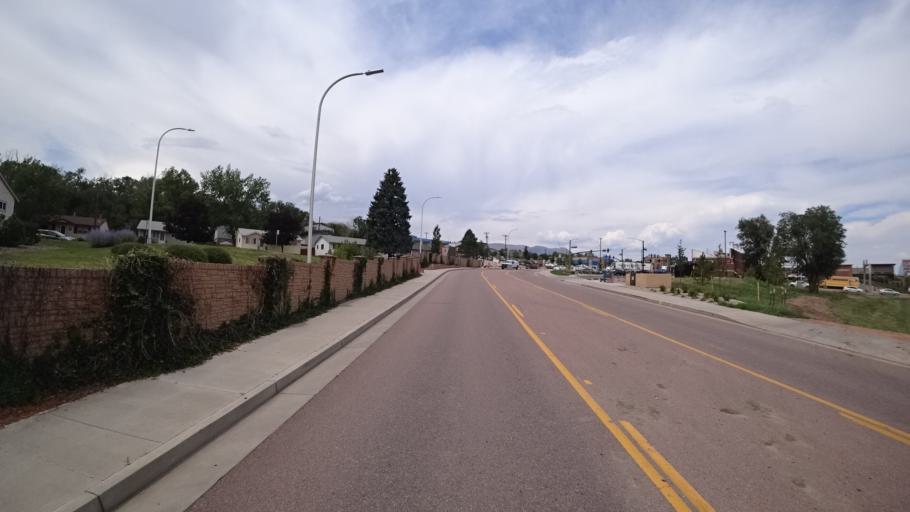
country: US
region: Colorado
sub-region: El Paso County
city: Colorado Springs
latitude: 38.8753
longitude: -104.8366
